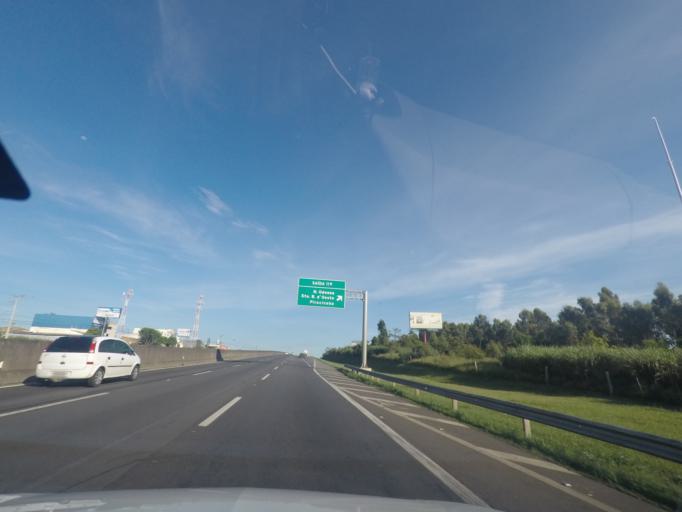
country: BR
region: Sao Paulo
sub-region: Nova Odessa
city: Nova Odessa
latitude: -22.7658
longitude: -47.2449
